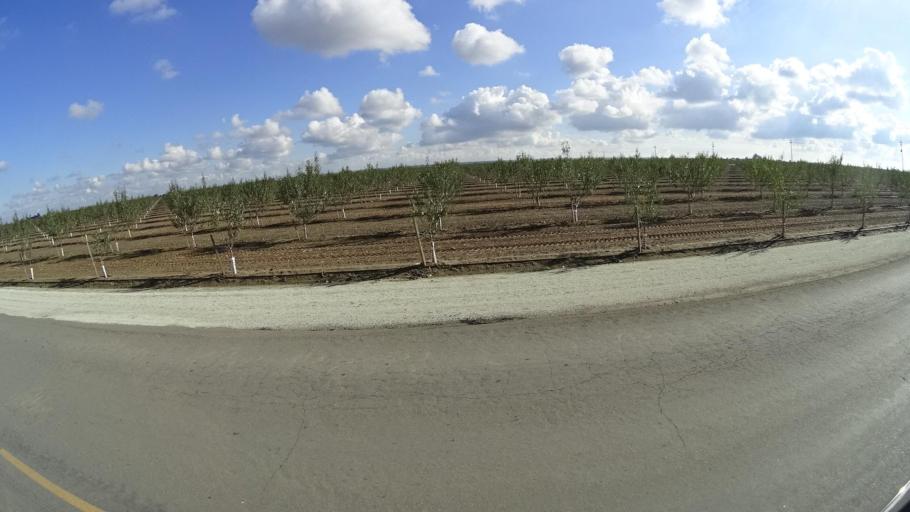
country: US
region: California
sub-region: Kern County
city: McFarland
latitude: 35.6541
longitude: -119.2322
